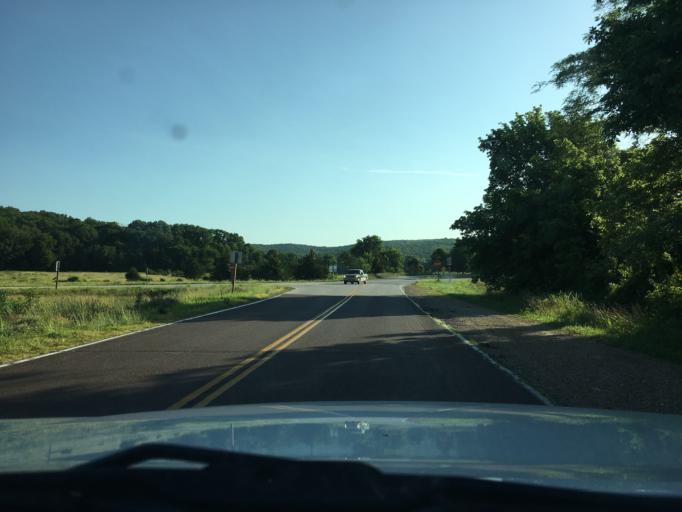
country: US
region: Missouri
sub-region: Gasconade County
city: Owensville
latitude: 38.4656
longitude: -91.6247
